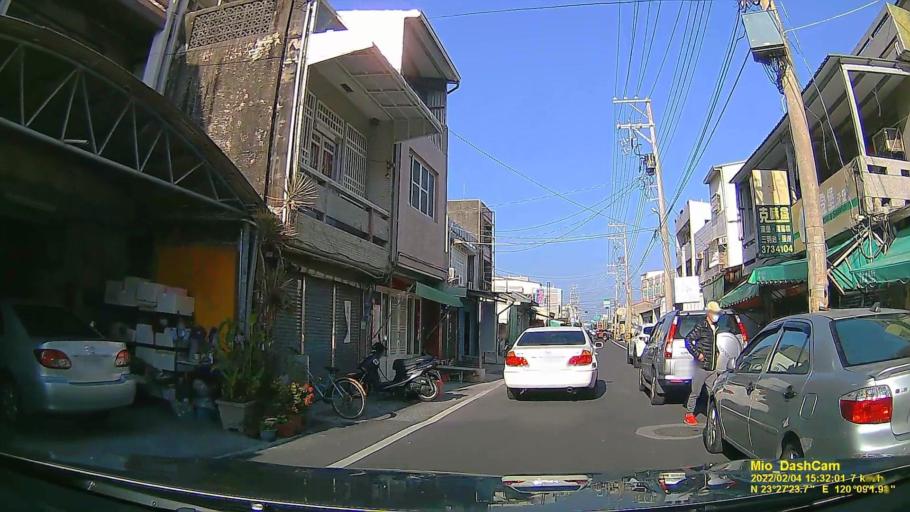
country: TW
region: Taiwan
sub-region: Chiayi
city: Taibao
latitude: 23.4566
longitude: 120.1505
